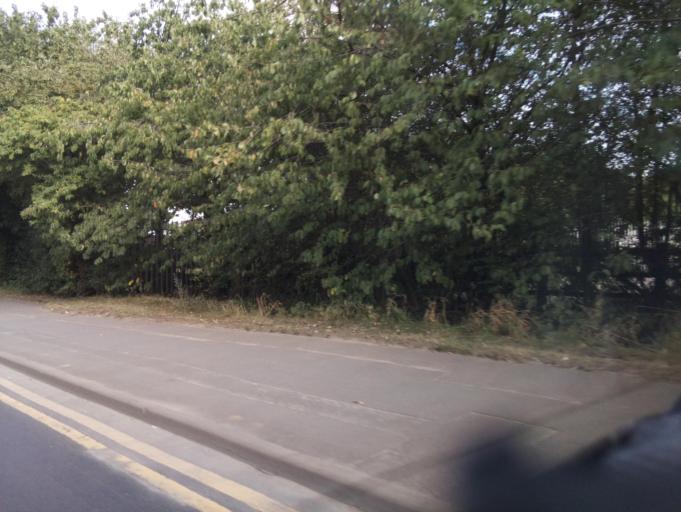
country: GB
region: England
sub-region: Staffordshire
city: Burton upon Trent
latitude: 52.7965
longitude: -1.6590
